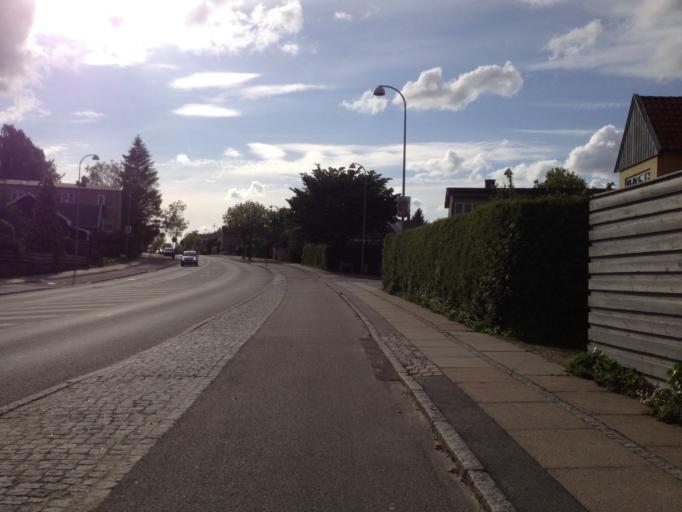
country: DK
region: Capital Region
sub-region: Gladsaxe Municipality
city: Buddinge
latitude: 55.7414
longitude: 12.5159
